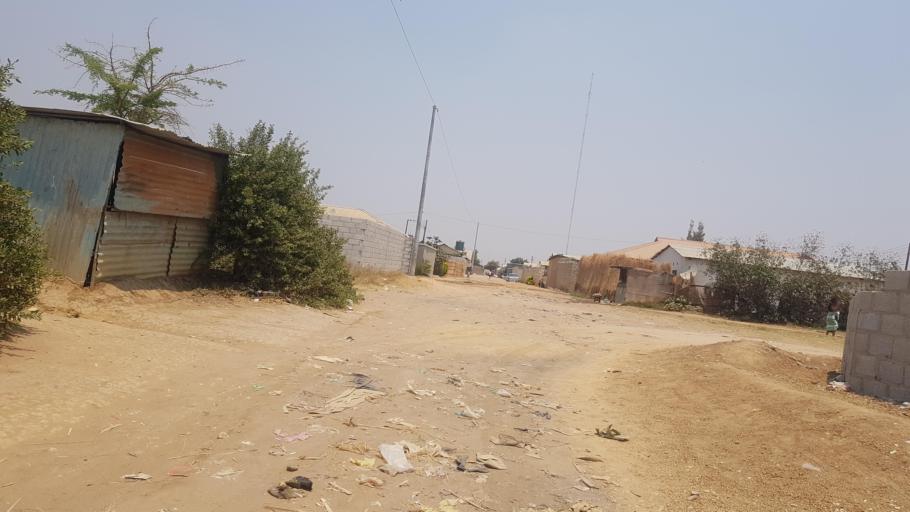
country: ZM
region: Lusaka
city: Lusaka
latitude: -15.4382
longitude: 28.3787
